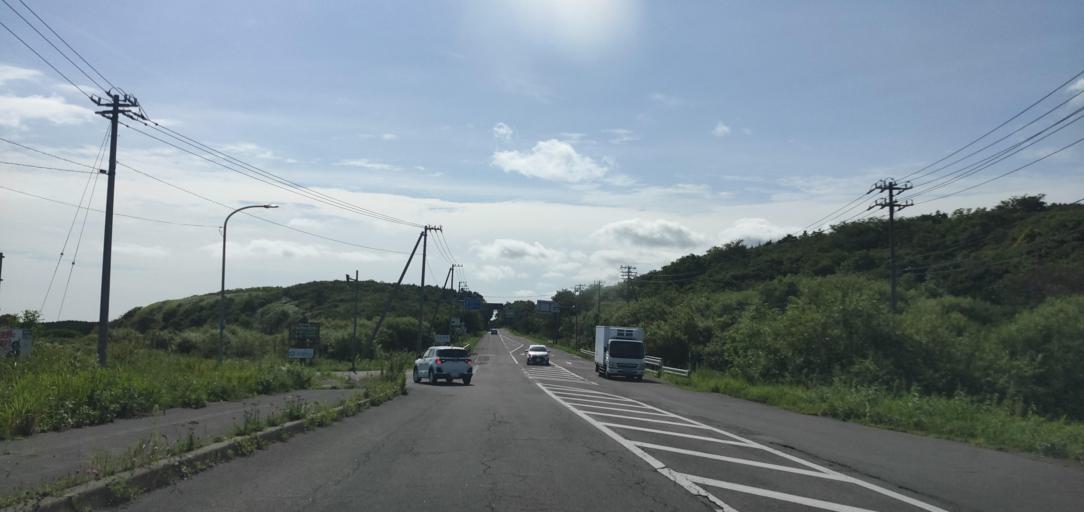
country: JP
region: Hokkaido
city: Shibetsu
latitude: 43.6388
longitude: 145.1626
